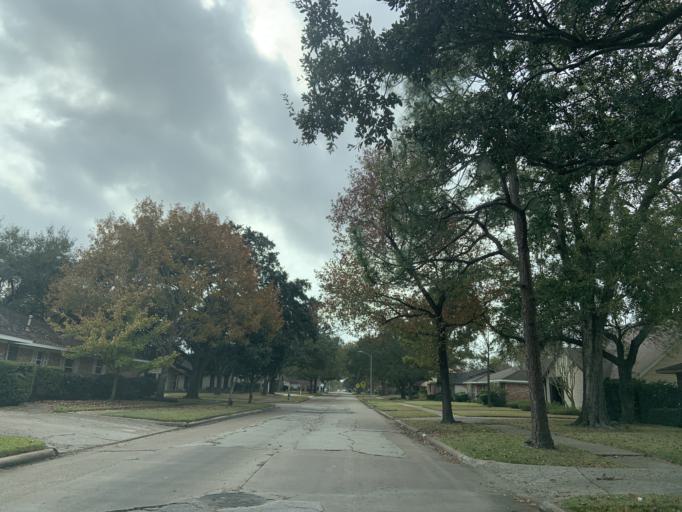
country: US
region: Texas
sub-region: Harris County
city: Bellaire
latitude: 29.6756
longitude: -95.5026
